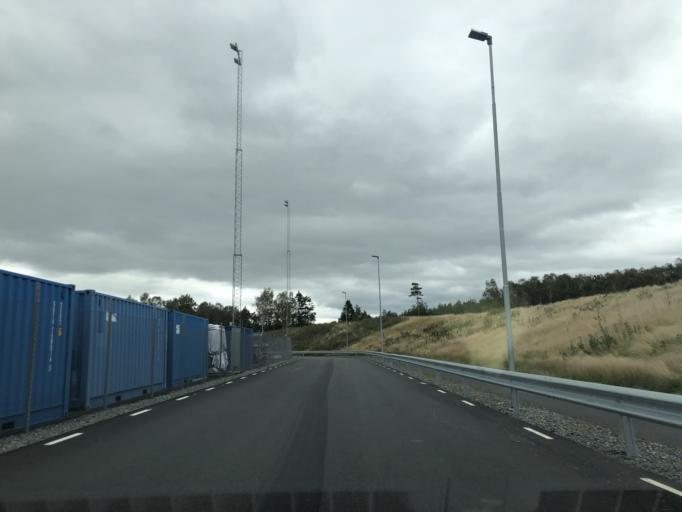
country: SE
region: Vaestra Goetaland
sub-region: Goteborg
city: Majorna
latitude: 57.7377
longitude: 11.8736
